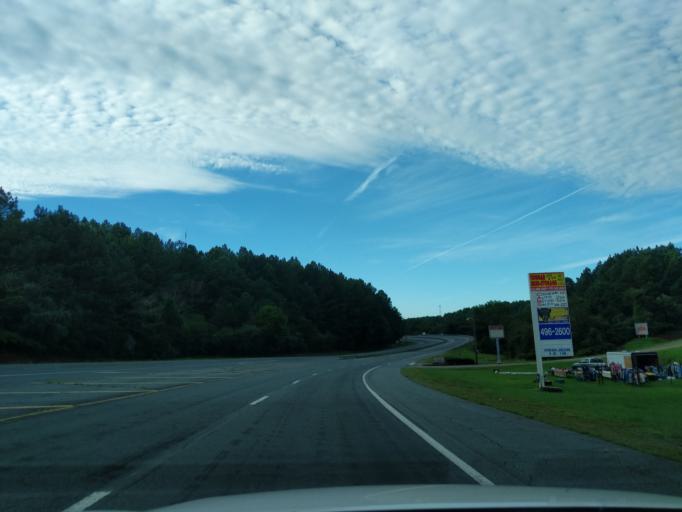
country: US
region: Georgia
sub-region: Fannin County
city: McCaysville
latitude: 35.0239
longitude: -84.3830
